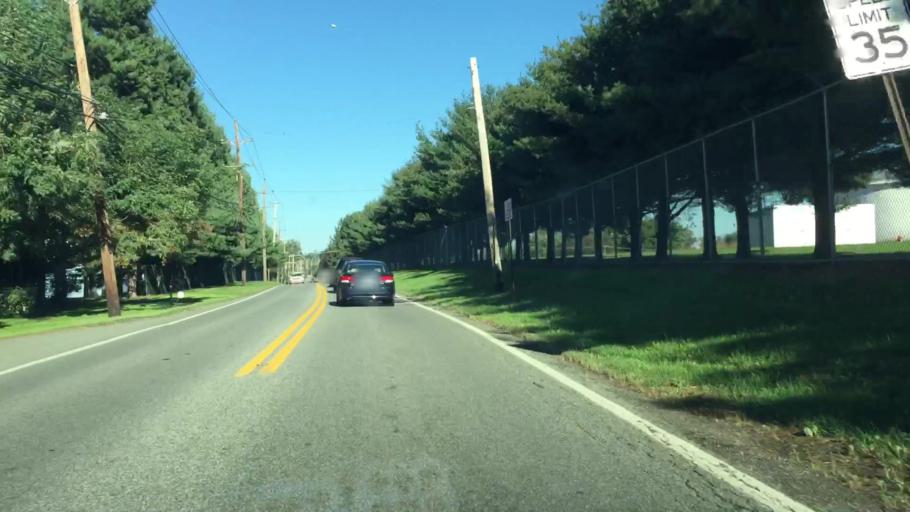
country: US
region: Pennsylvania
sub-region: Delaware County
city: Chester Heights
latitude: 39.8682
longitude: -75.4574
